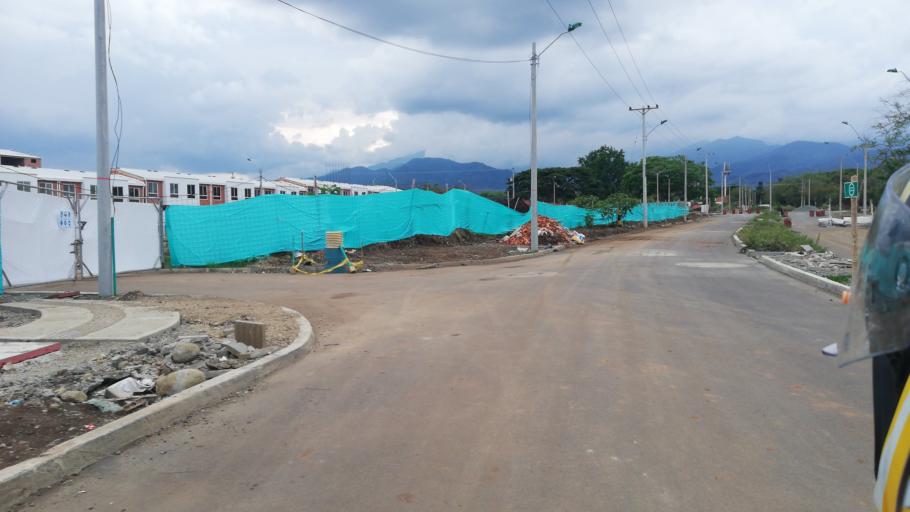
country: CO
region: Valle del Cauca
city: Jamundi
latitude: 3.3466
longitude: -76.5199
